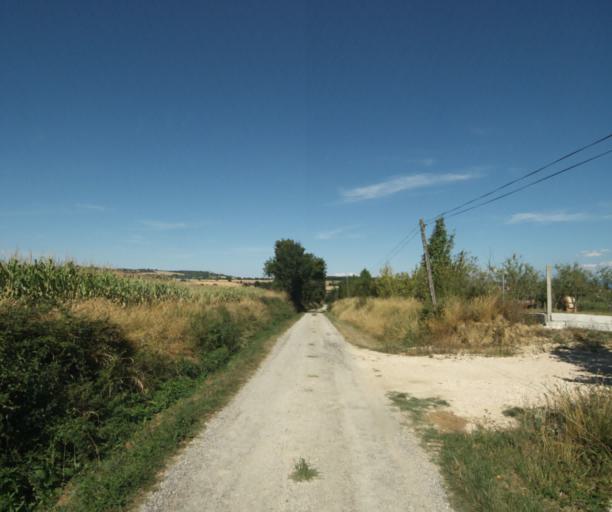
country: FR
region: Midi-Pyrenees
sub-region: Departement de la Haute-Garonne
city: Saint-Felix-Lauragais
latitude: 43.4927
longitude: 1.9050
